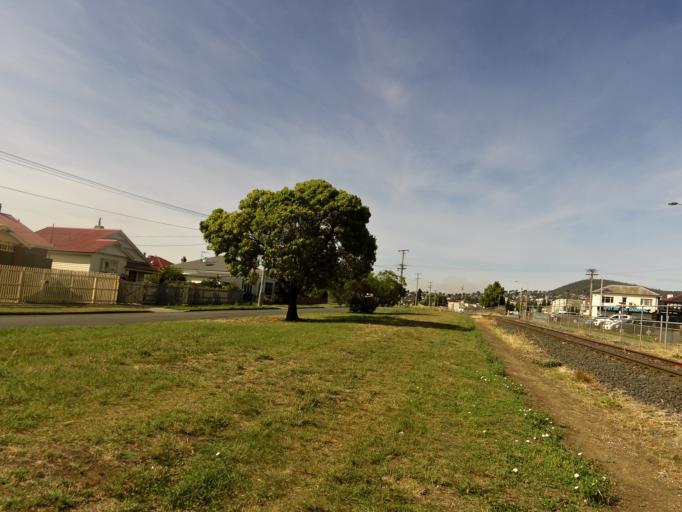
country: AU
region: Tasmania
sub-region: Glenorchy
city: Moonah
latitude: -42.8469
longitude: 147.2983
